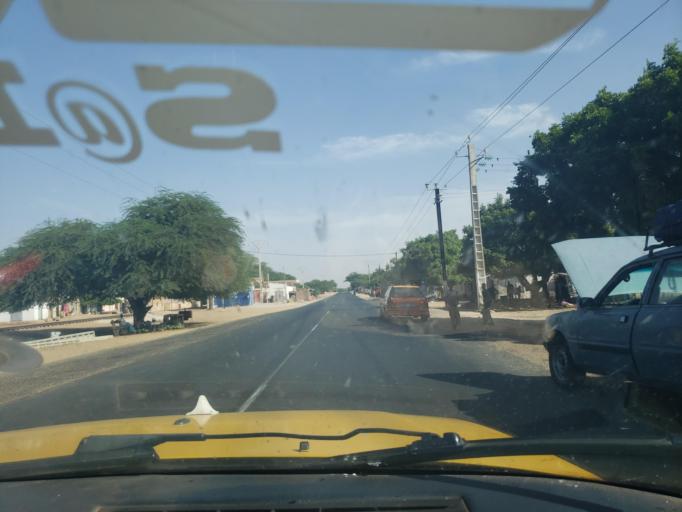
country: SN
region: Saint-Louis
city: Saint-Louis
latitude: 15.9285
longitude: -16.3246
